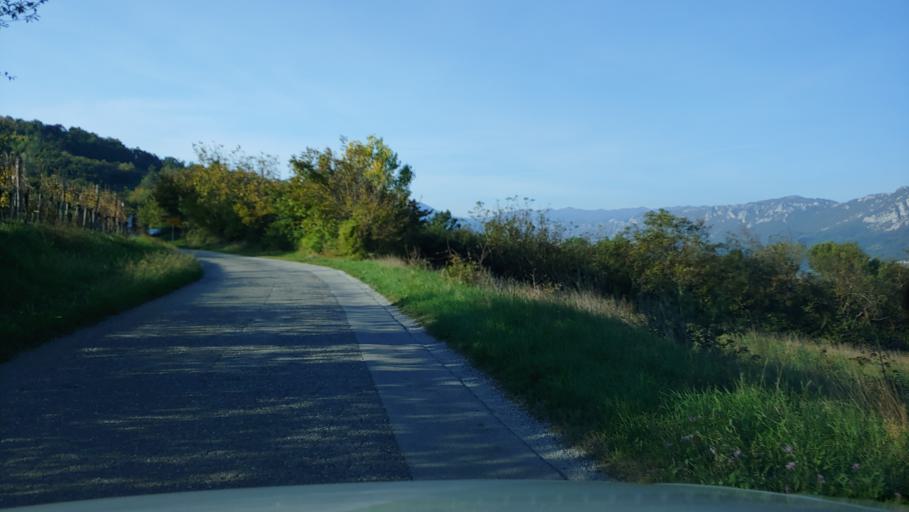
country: SI
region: Vipava
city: Vipava
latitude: 45.8236
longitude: 13.9398
